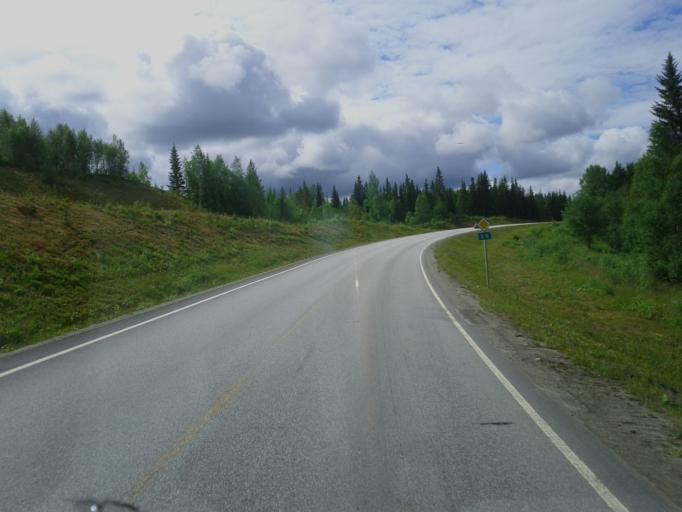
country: NO
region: Nord-Trondelag
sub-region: Namsskogan
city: Namsskogan
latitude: 64.7119
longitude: 12.7957
